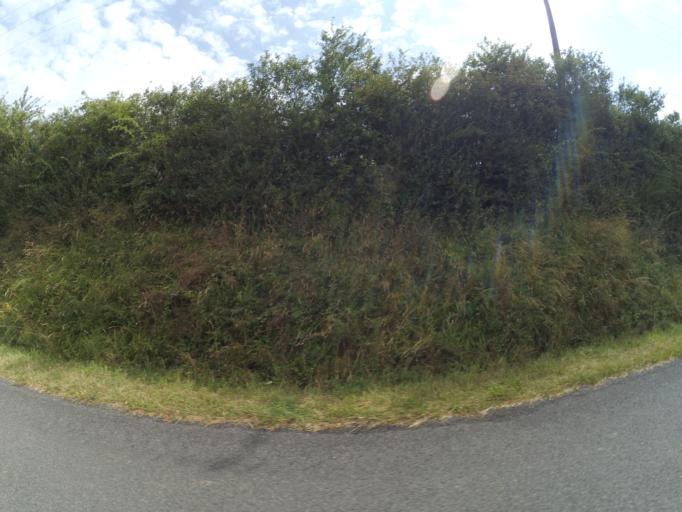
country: FR
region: Pays de la Loire
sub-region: Departement de Maine-et-Loire
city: Nueil-sur-Layon
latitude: 47.1839
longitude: -0.3526
